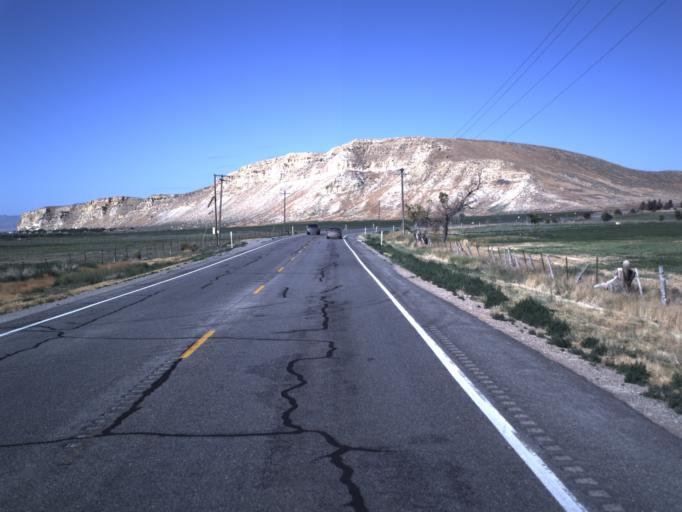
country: US
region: Utah
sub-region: Sanpete County
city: Gunnison
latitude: 39.1566
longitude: -111.7615
